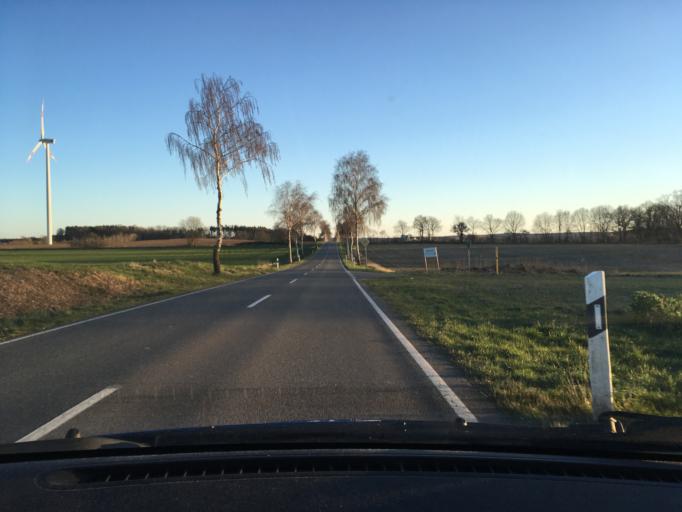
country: DE
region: Lower Saxony
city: Dahlem
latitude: 53.2055
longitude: 10.7521
